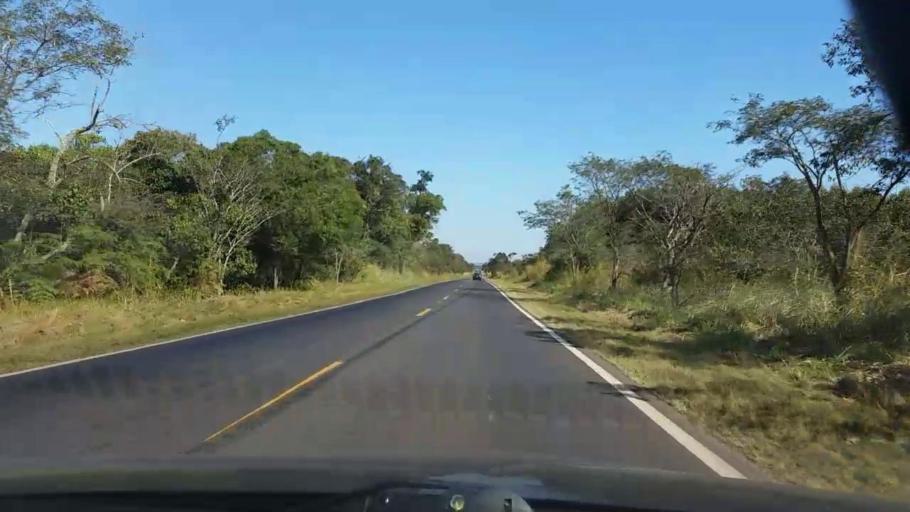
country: BR
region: Sao Paulo
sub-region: Sao Manuel
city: Sao Manuel
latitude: -22.8940
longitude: -48.7629
